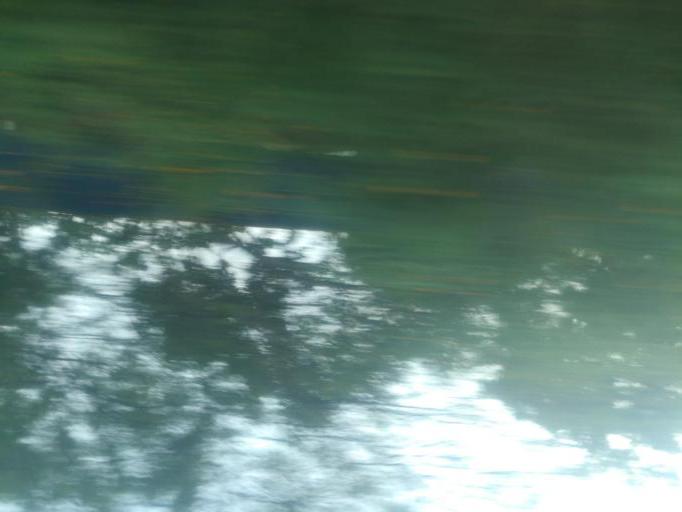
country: NG
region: Ogun
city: Abeokuta
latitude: 7.1621
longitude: 3.2669
